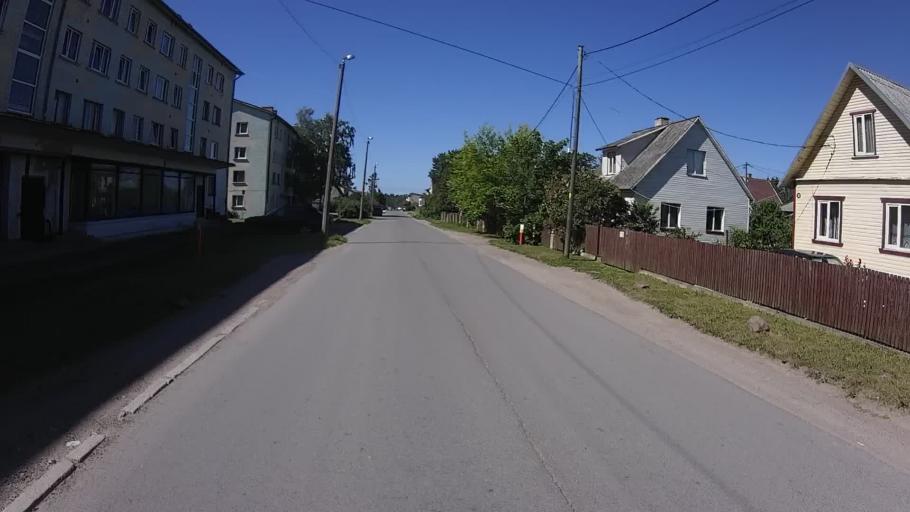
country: EE
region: Ida-Virumaa
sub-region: Kohtla-Jaerve linn
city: Kohtla-Jarve
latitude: 59.4055
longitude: 27.2968
